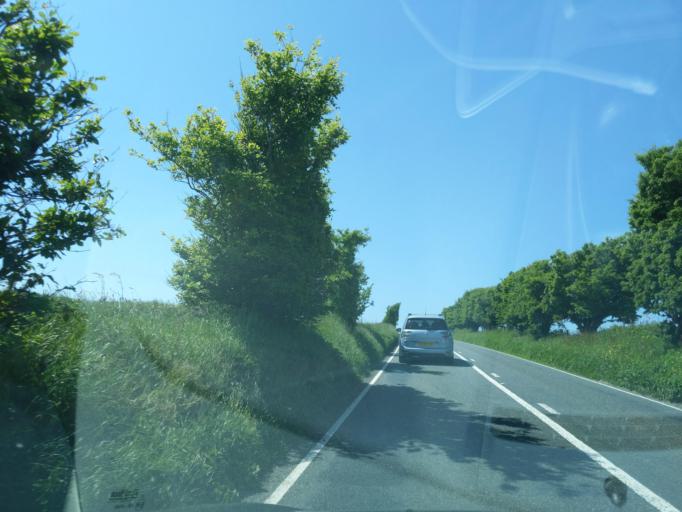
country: GB
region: England
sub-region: Cornwall
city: Jacobstow
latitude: 50.6520
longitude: -4.5456
